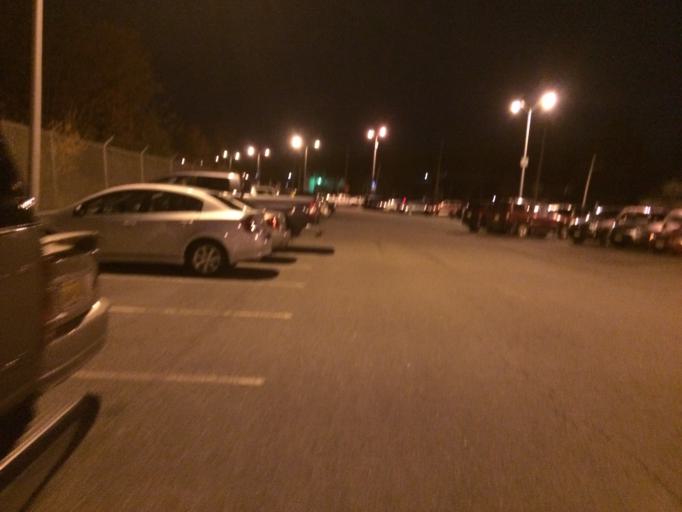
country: US
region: New Jersey
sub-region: Camden County
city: Lindenwold
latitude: 39.8319
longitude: -74.9992
